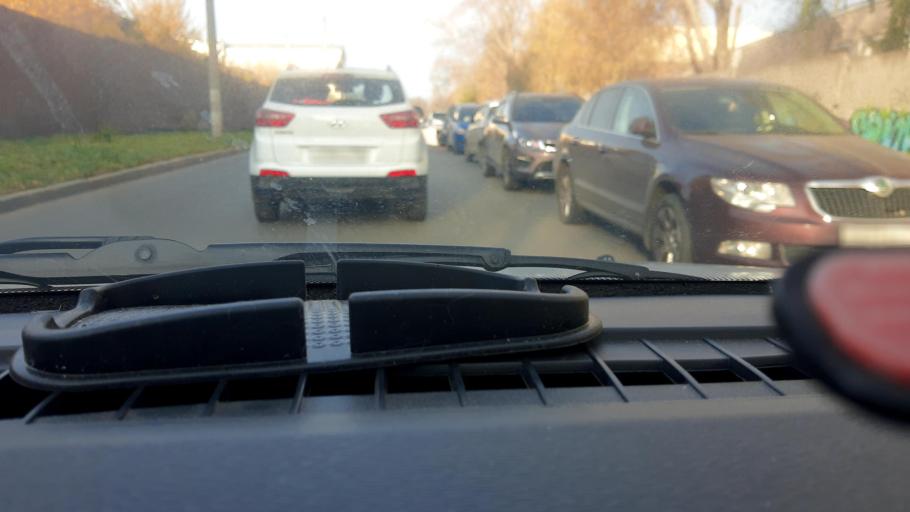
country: RU
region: Nizjnij Novgorod
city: Nizhniy Novgorod
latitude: 56.2510
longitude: 43.9721
